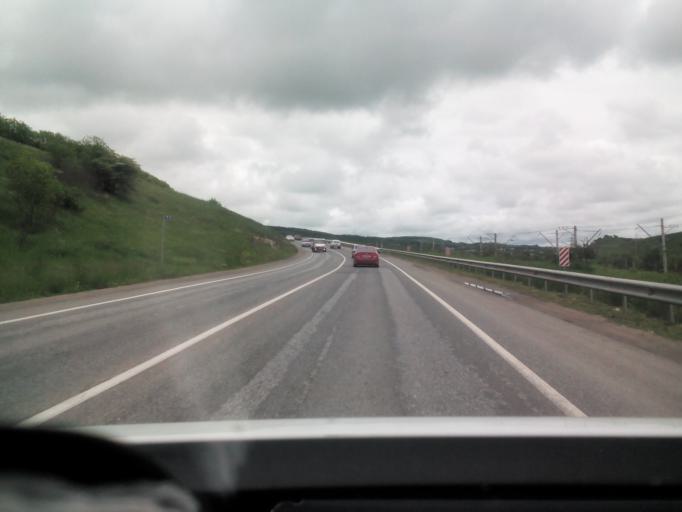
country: RU
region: Stavropol'skiy
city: Yasnaya Polyana
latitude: 43.9967
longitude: 42.7951
